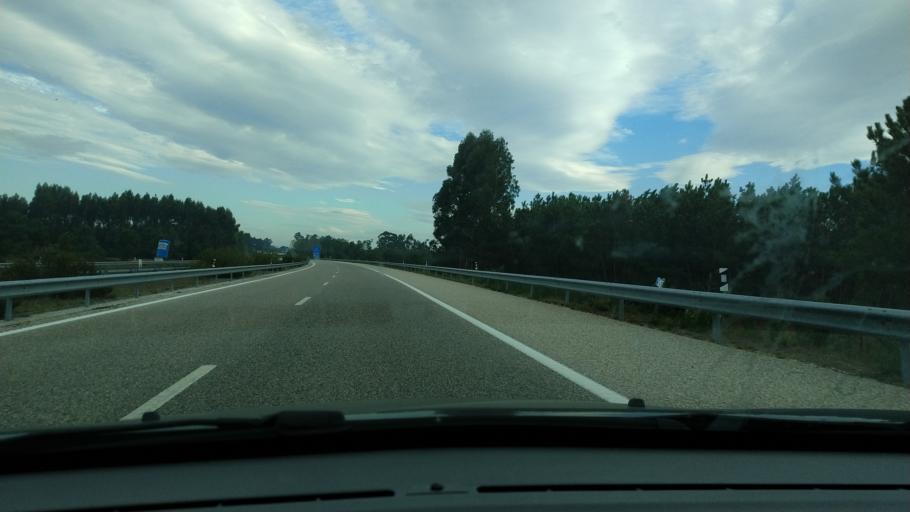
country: PT
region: Aveiro
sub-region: Vagos
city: Vagos
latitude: 40.4872
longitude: -8.6815
